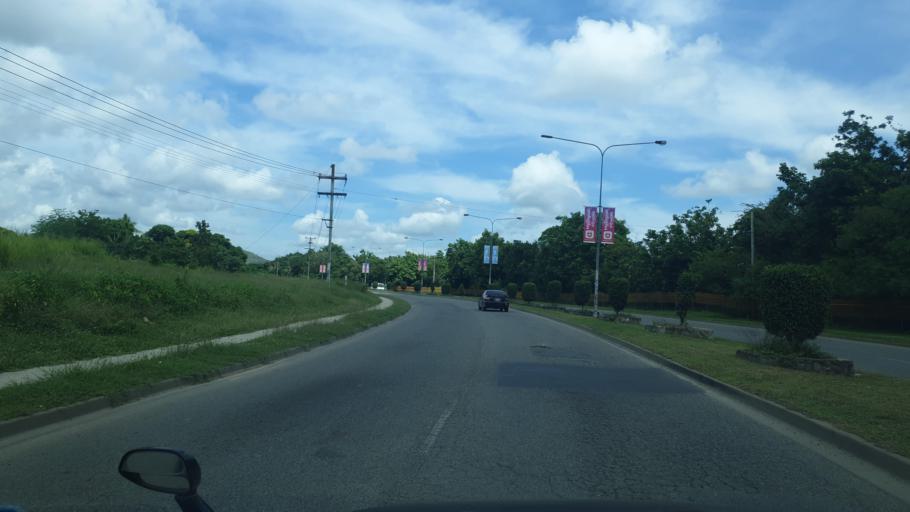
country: PG
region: National Capital
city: Port Moresby
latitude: -9.4053
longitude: 147.1645
